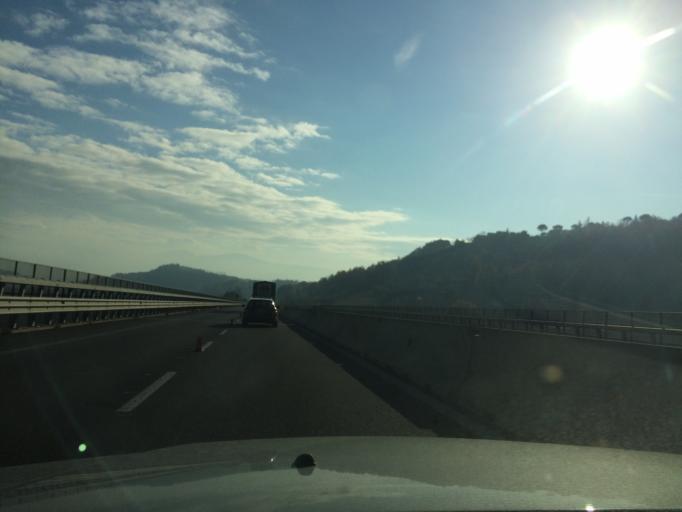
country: IT
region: Umbria
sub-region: Provincia di Terni
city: San Gemini
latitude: 42.6164
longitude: 12.5540
